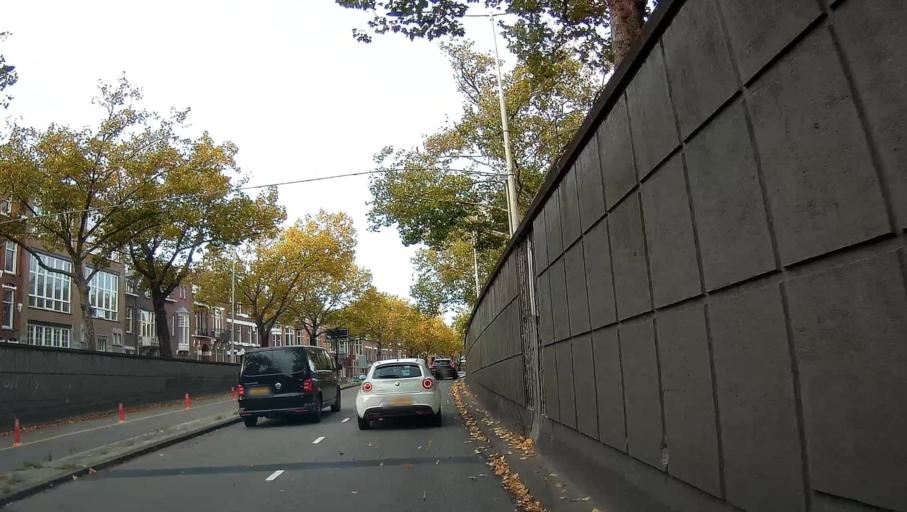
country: NL
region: South Holland
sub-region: Gemeente Rotterdam
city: Delfshaven
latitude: 51.9156
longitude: 4.4630
